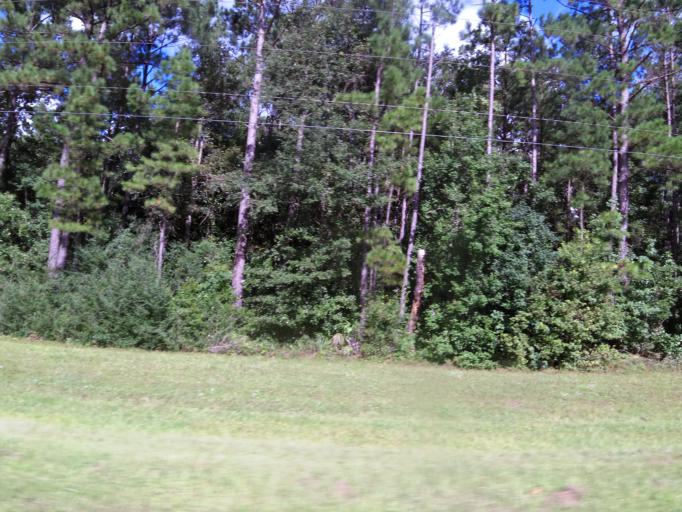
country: US
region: Georgia
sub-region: Camden County
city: Kingsland
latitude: 30.7862
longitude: -81.6874
